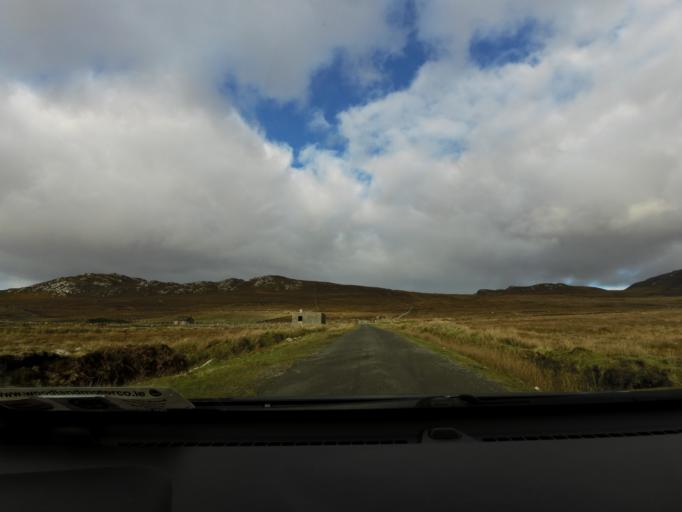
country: IE
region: Connaught
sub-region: Maigh Eo
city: Belmullet
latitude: 53.8905
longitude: -9.9846
